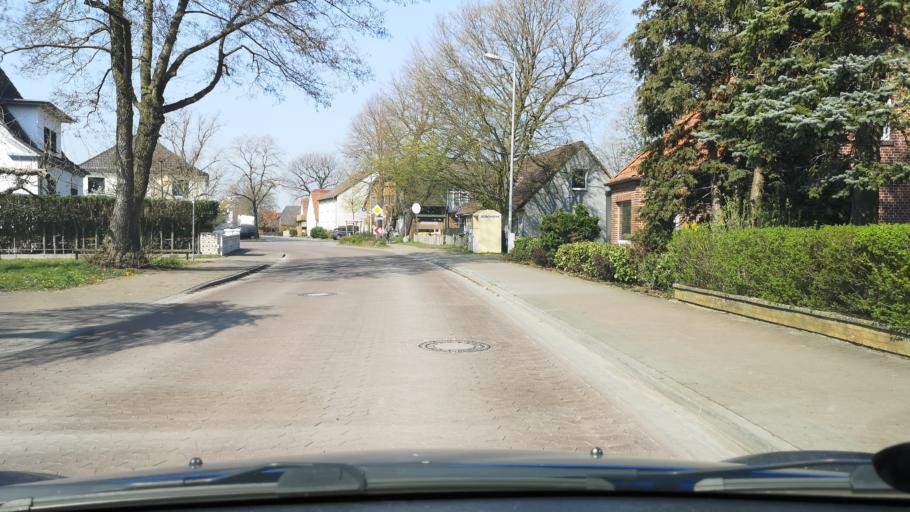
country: DE
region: Lower Saxony
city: Neustadt am Rubenberge
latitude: 52.5137
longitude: 9.5270
